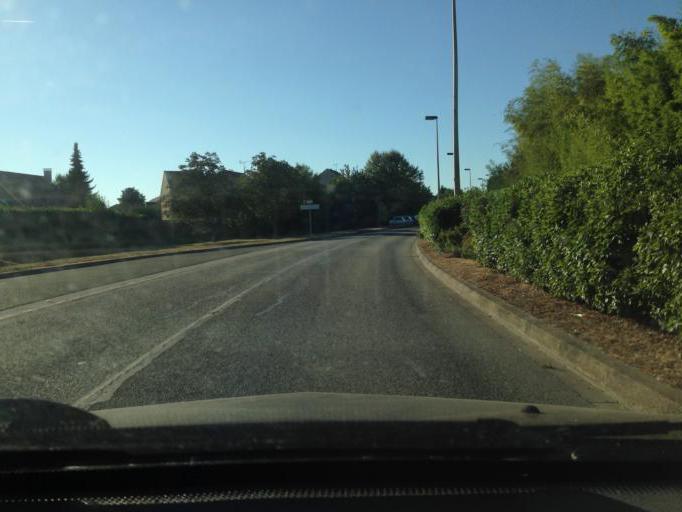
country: FR
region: Ile-de-France
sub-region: Departement des Yvelines
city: Chateaufort
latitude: 48.7206
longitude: 2.0857
